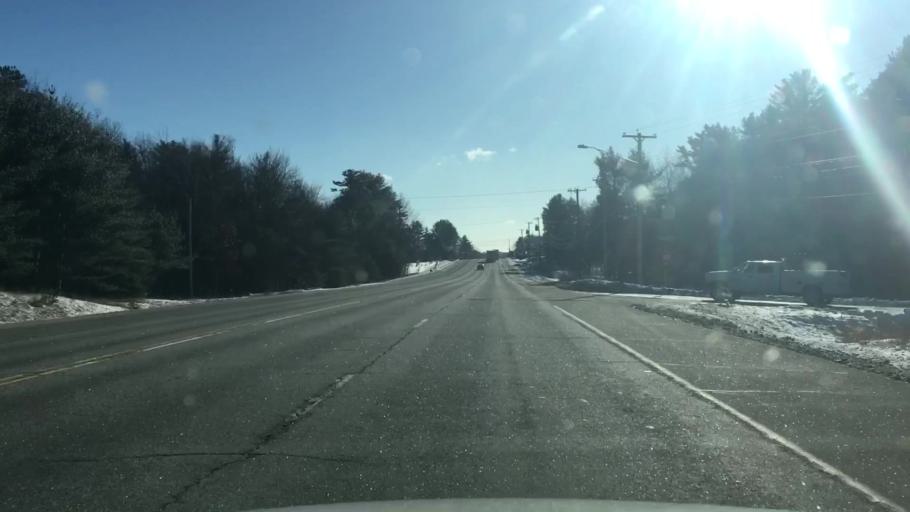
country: US
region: Maine
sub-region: Androscoggin County
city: Lewiston
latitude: 44.1746
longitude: -70.2321
